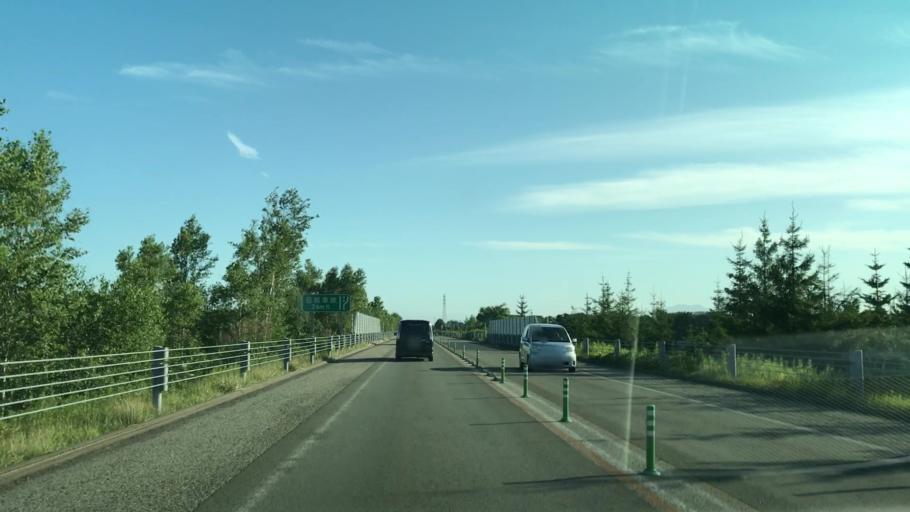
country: JP
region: Hokkaido
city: Chitose
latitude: 42.8705
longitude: 141.6129
